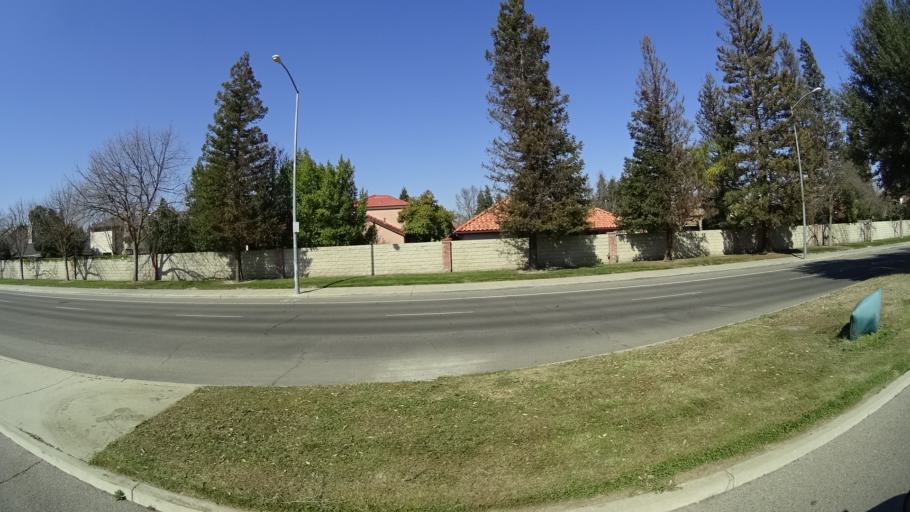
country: US
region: California
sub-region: Fresno County
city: Clovis
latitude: 36.8774
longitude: -119.7757
